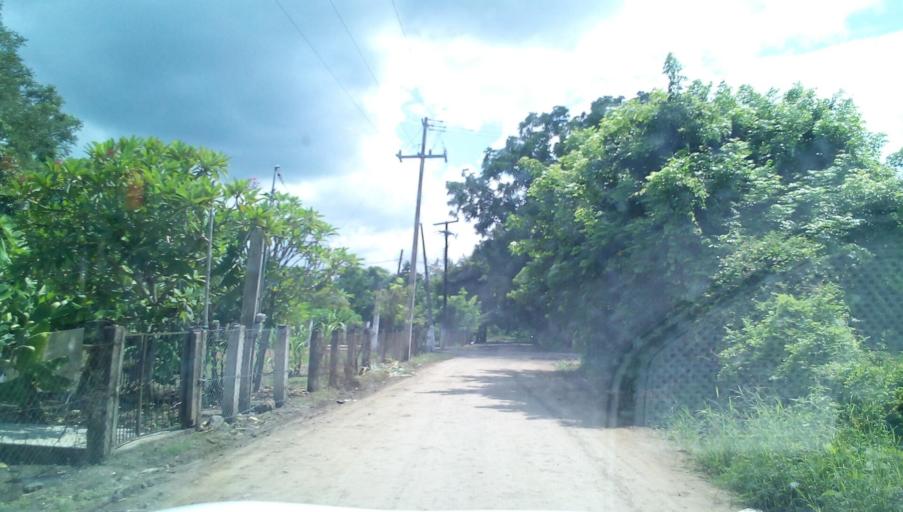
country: MX
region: Veracruz
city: Tamalin
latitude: 21.3571
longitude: -97.7965
